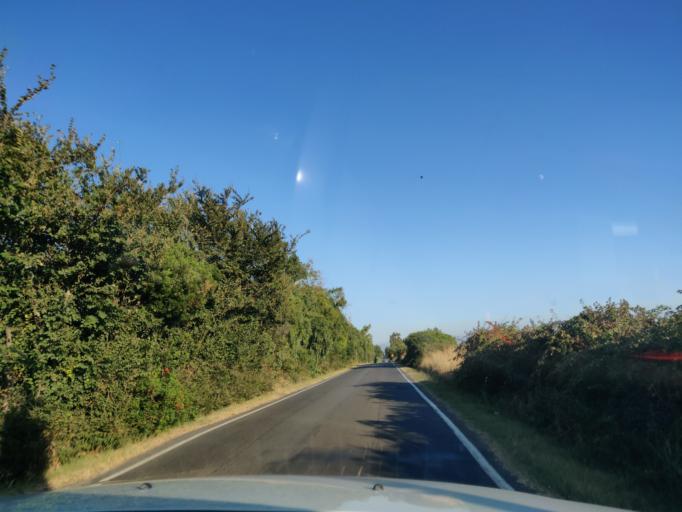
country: IT
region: Latium
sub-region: Provincia di Viterbo
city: Tarquinia
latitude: 42.2746
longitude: 11.6833
